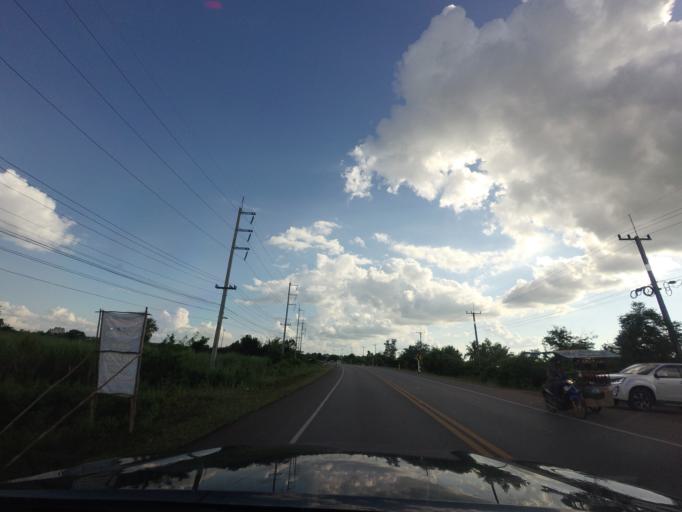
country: TH
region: Changwat Udon Thani
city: Thung Fon
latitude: 17.5149
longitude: 103.2040
